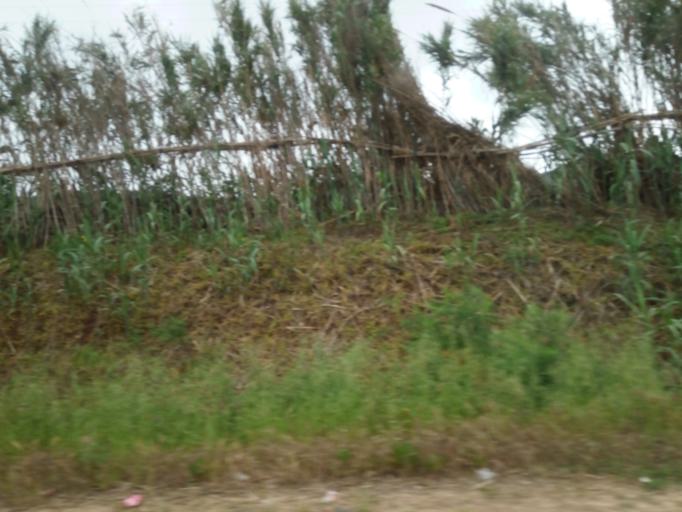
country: DZ
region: Tipaza
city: Tipasa
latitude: 36.5894
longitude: 2.5287
